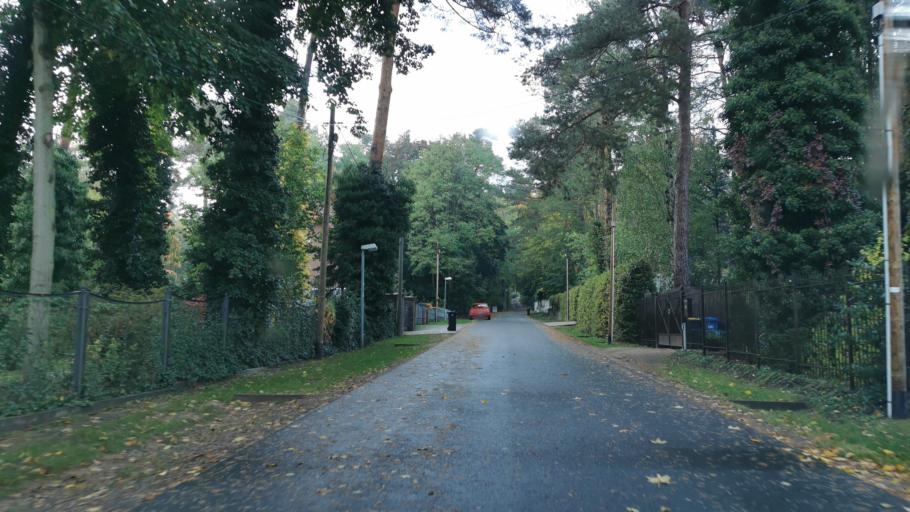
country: DE
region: Brandenburg
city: Michendorf
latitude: 52.3323
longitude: 13.0601
